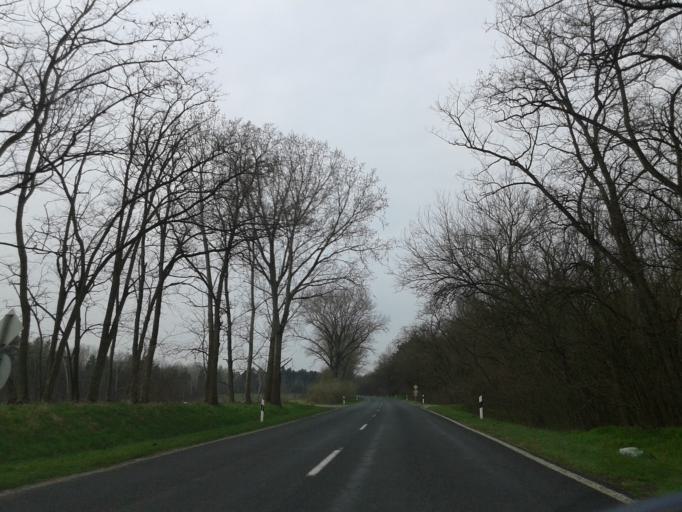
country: HU
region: Komarom-Esztergom
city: Acs
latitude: 47.7393
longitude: 17.9372
